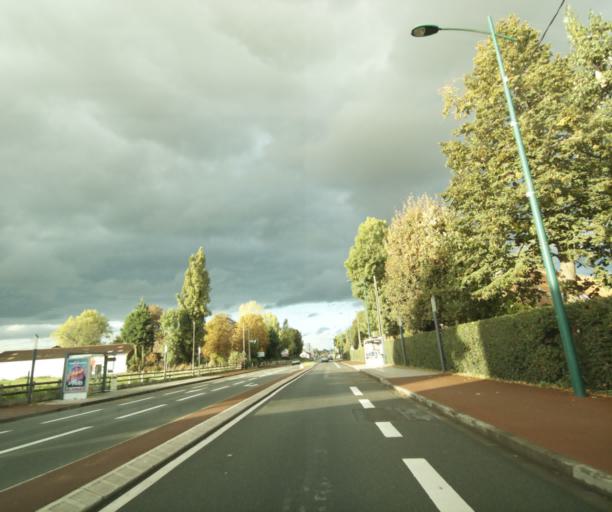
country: FR
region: Nord-Pas-de-Calais
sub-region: Departement du Nord
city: Roncq
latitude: 50.7592
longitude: 3.1210
